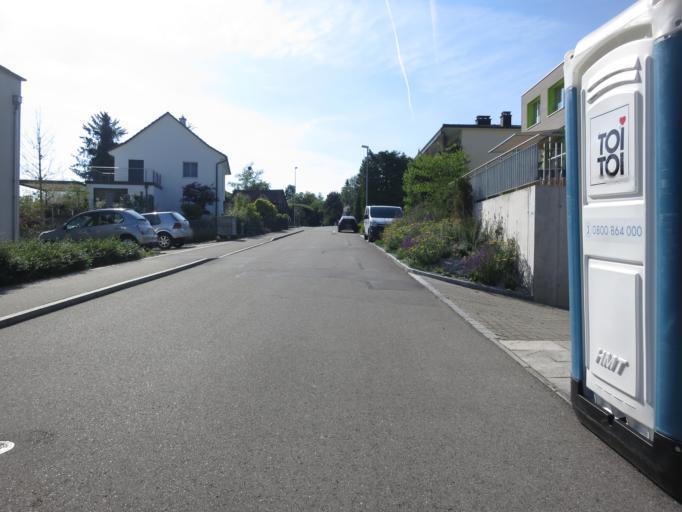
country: CH
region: Zurich
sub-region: Bezirk Meilen
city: Stafa
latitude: 47.2445
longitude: 8.7244
